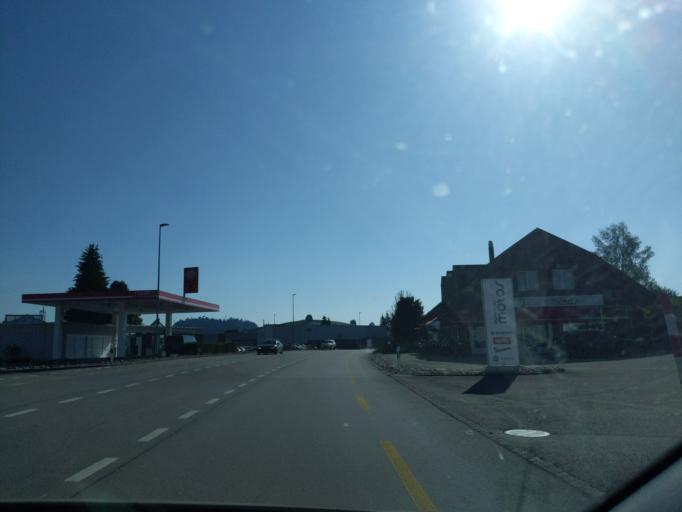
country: CH
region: Bern
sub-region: Oberaargau
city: Huttwil
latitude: 47.1150
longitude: 7.8657
